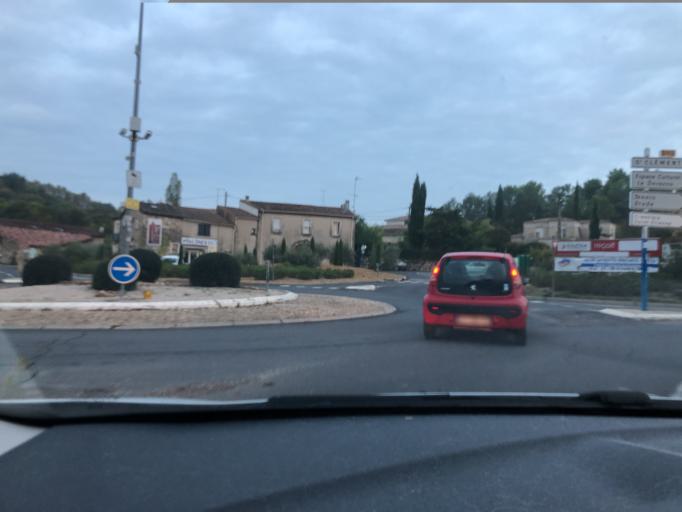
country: FR
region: Languedoc-Roussillon
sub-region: Departement de l'Herault
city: Montferrier-sur-Lez
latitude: 43.6708
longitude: 3.8619
